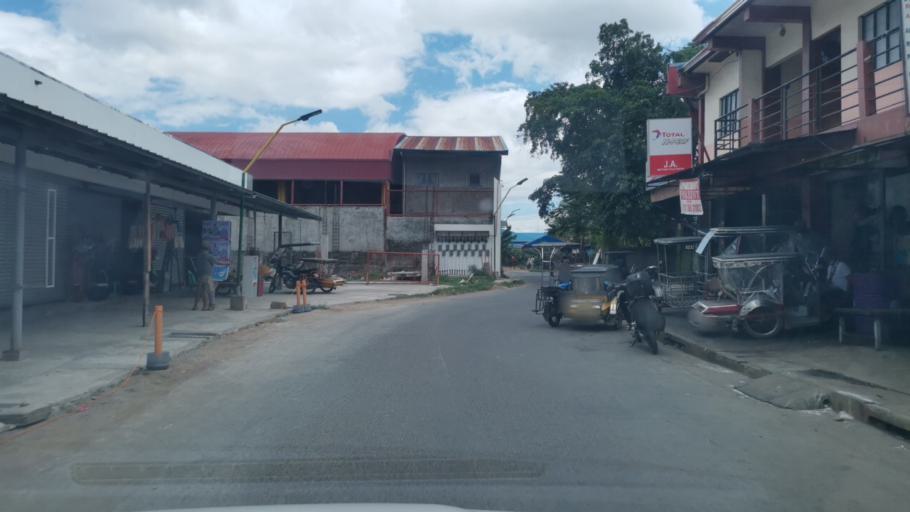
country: PH
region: Calabarzon
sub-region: Province of Batangas
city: Tanauan
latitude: 14.0822
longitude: 121.1436
